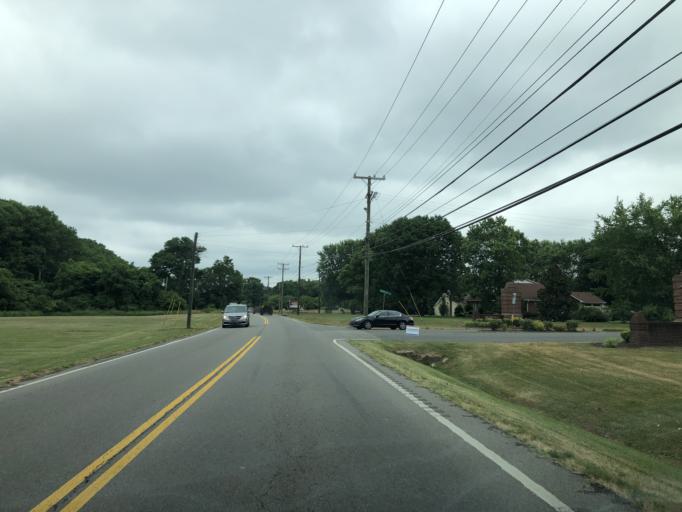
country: US
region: Tennessee
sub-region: Davidson County
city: Goodlettsville
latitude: 36.2789
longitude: -86.7739
